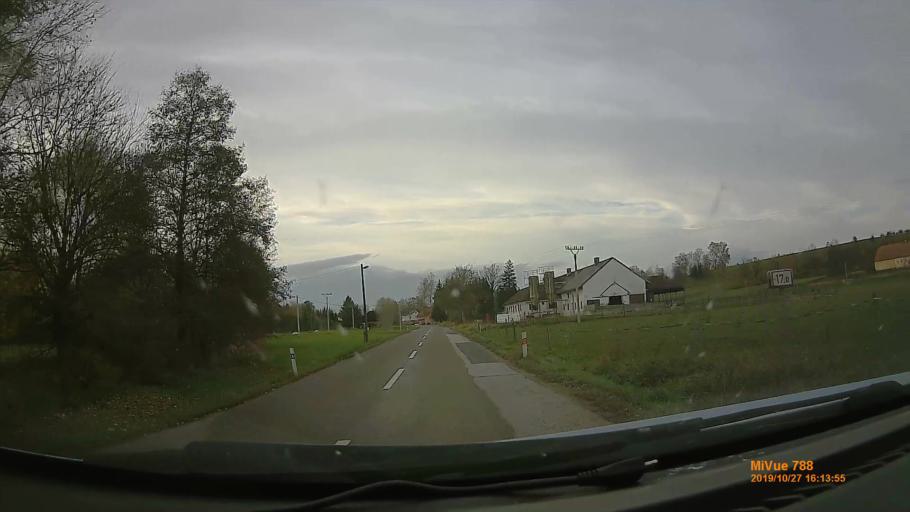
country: PL
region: Lower Silesian Voivodeship
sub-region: Powiat klodzki
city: Radkow
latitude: 50.5521
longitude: 16.3994
